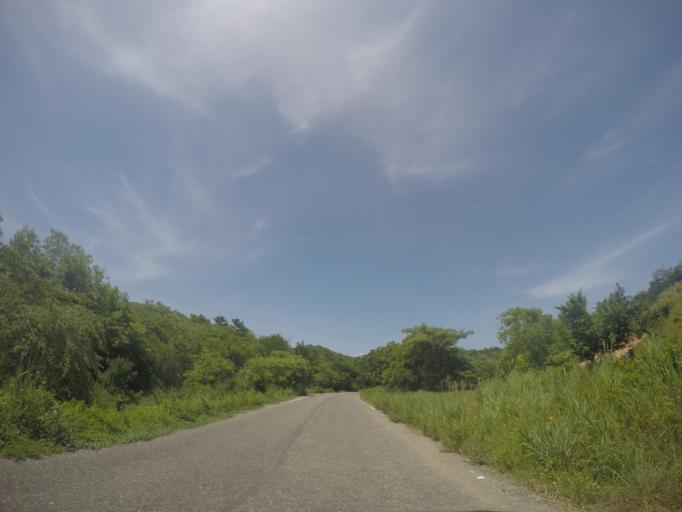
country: MX
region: Oaxaca
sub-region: Villa de Tututepec de Melchor Ocampo
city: Santa Rosa de Lima
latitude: 15.9926
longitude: -97.5353
